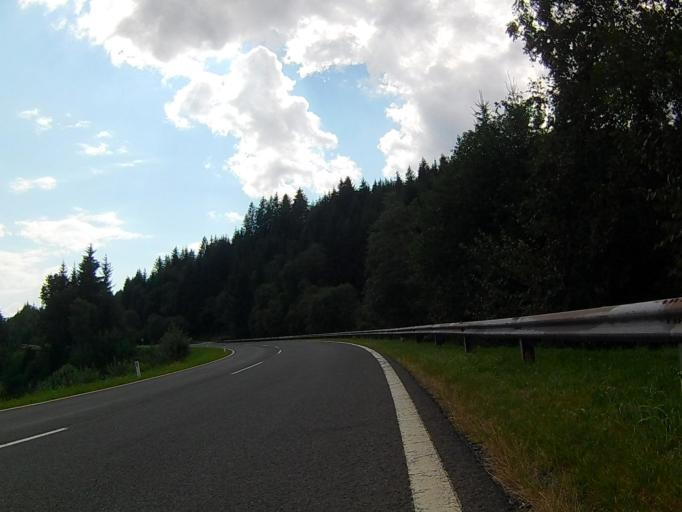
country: AT
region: Styria
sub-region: Politischer Bezirk Deutschlandsberg
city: Soboth
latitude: 46.6838
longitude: 15.0543
